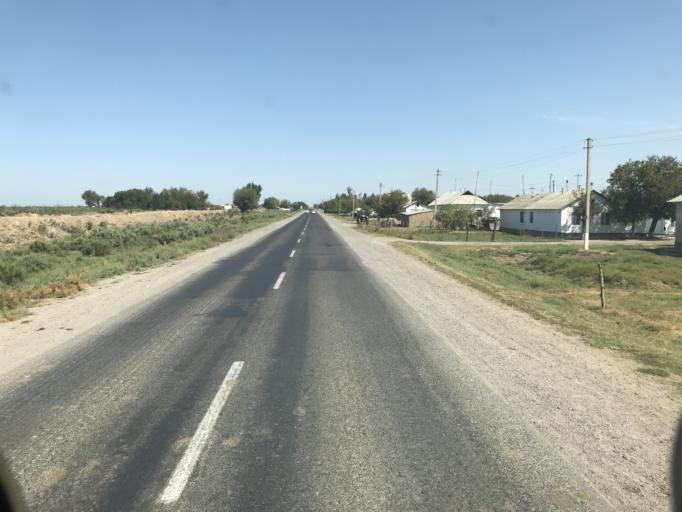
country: KZ
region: Ongtustik Qazaqstan
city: Myrzakent
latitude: 40.7563
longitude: 68.5370
